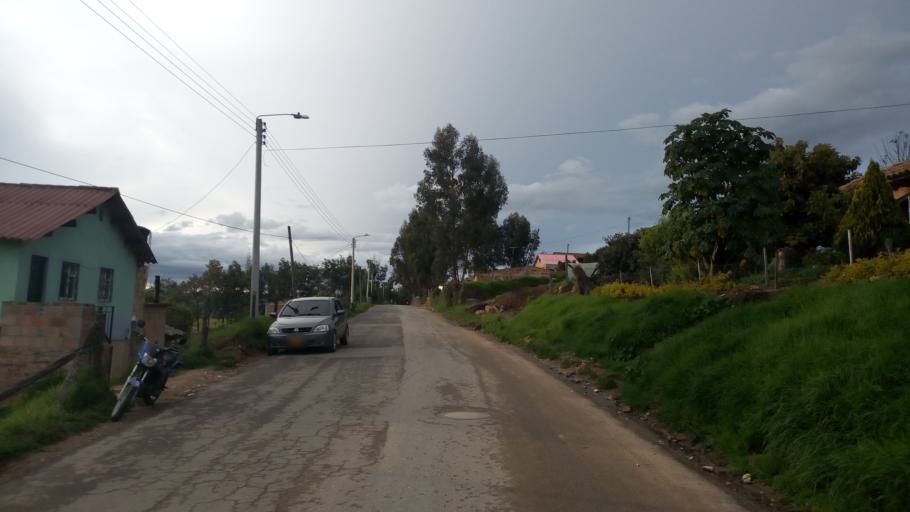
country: CO
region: Boyaca
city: Toca
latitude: 5.5731
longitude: -73.1838
